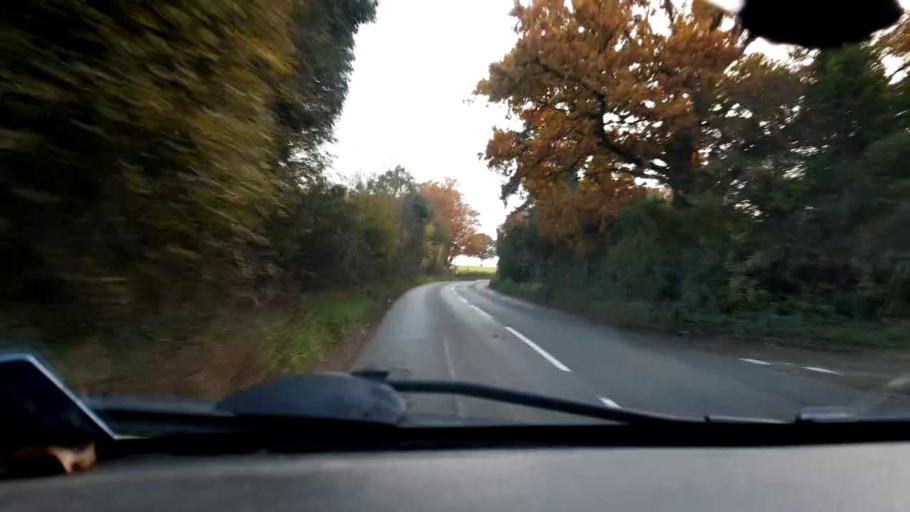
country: GB
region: England
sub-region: Norfolk
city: Mattishall
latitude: 52.7129
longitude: 1.1094
